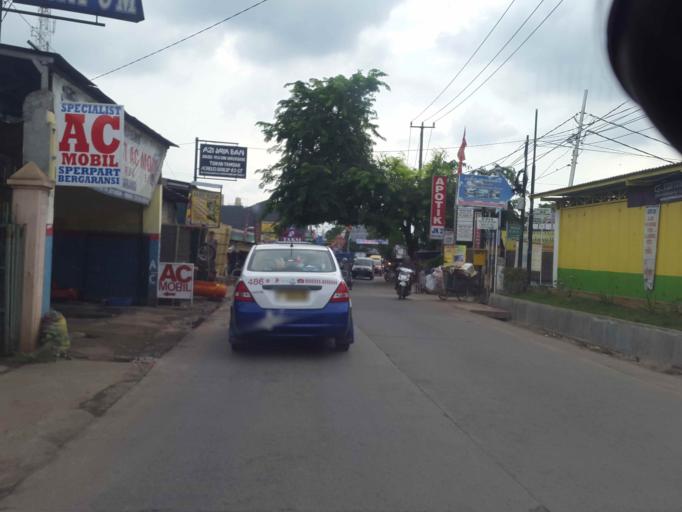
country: ID
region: West Java
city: Bekasi
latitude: -6.3063
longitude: 106.9558
